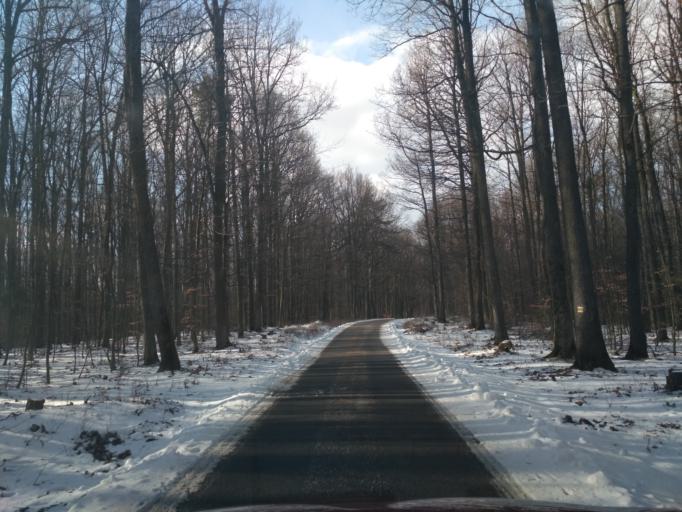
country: SK
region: Kosicky
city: Kosice
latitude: 48.7244
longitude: 21.1846
